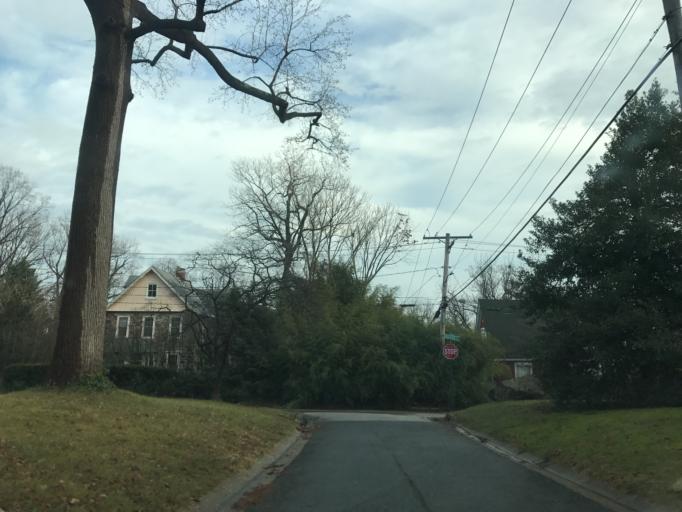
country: US
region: Maryland
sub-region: Baltimore County
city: Overlea
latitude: 39.3507
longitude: -76.5399
